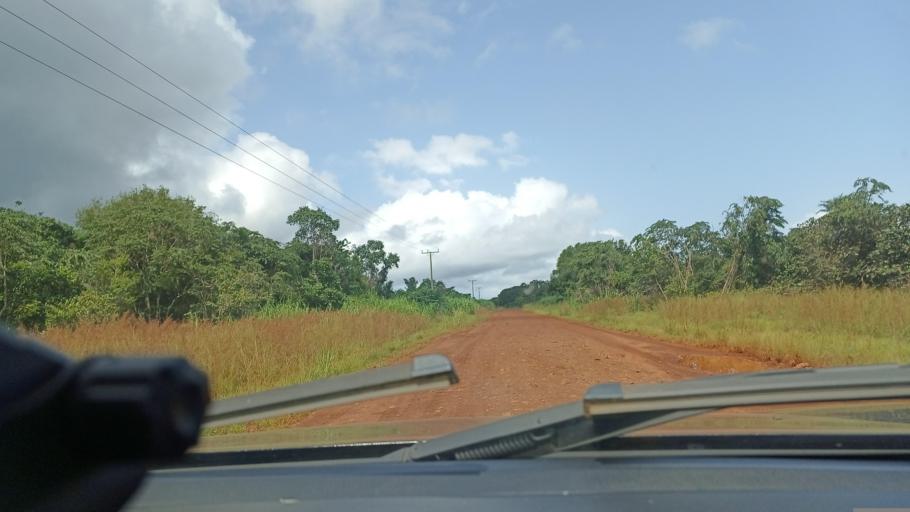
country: LR
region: Grand Cape Mount
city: Robertsport
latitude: 6.6899
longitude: -11.2596
